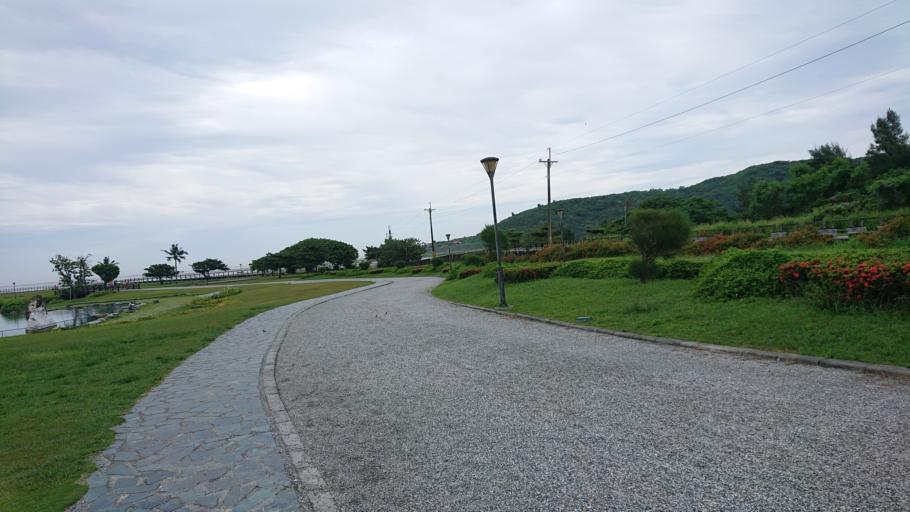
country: TW
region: Taiwan
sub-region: Hualien
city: Hualian
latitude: 23.9374
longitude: 121.6008
